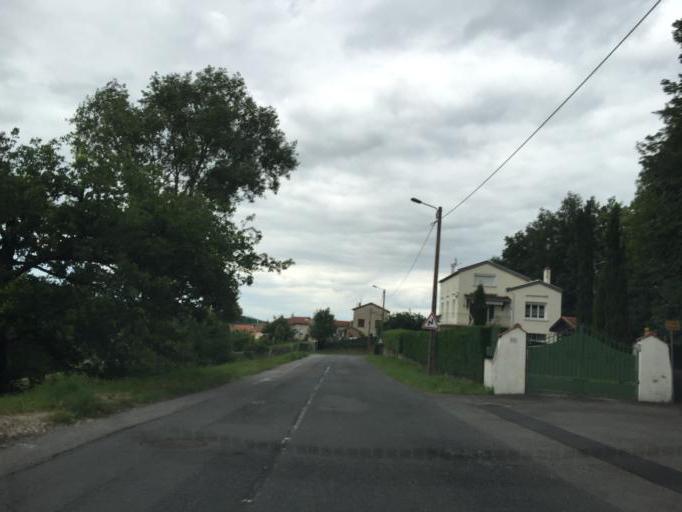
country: FR
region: Rhone-Alpes
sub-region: Departement de la Loire
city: Saint-Jean-Bonnefonds
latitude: 45.4346
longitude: 4.4527
